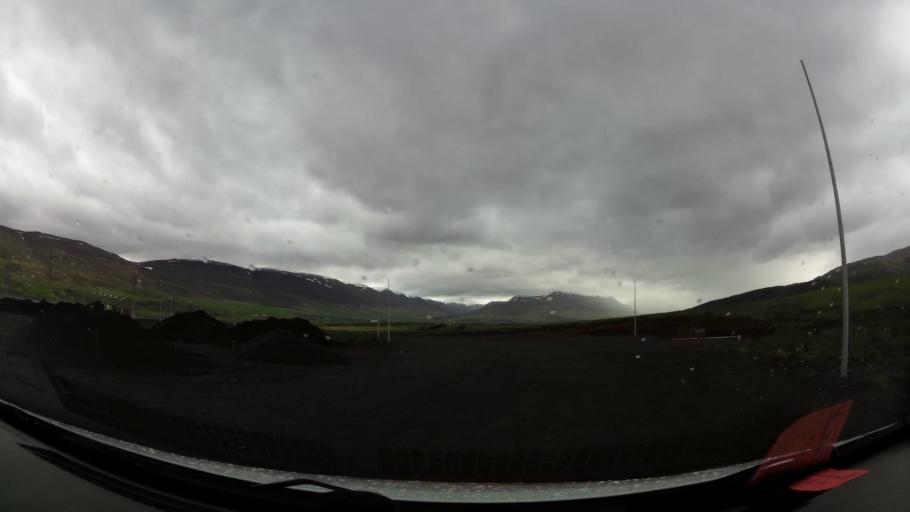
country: IS
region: Northeast
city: Akureyri
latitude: 65.6597
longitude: -18.0974
